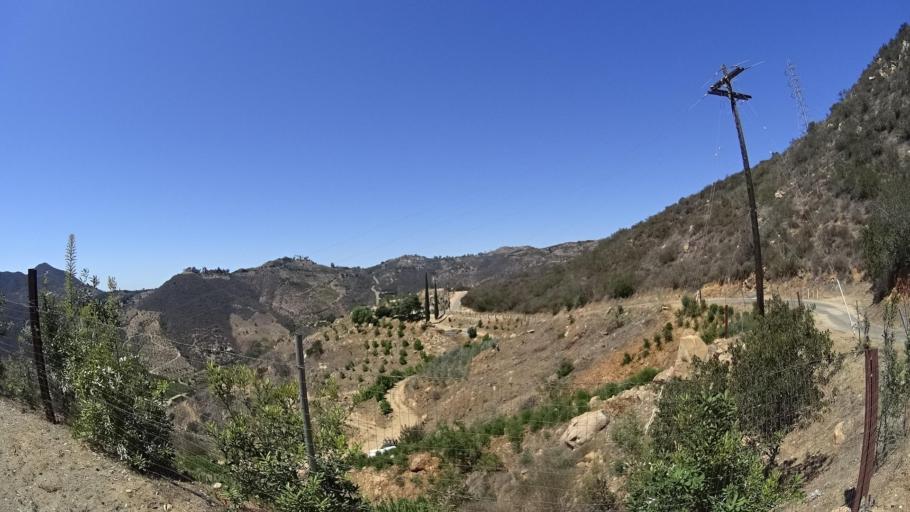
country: US
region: California
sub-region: San Diego County
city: Rainbow
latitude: 33.3877
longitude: -117.1025
